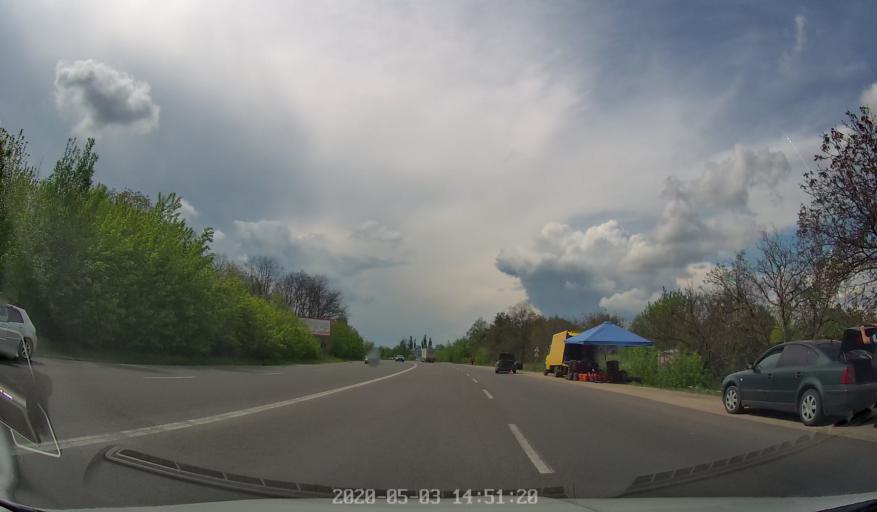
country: MD
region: Chisinau
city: Vatra
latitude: 47.0583
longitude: 28.7579
